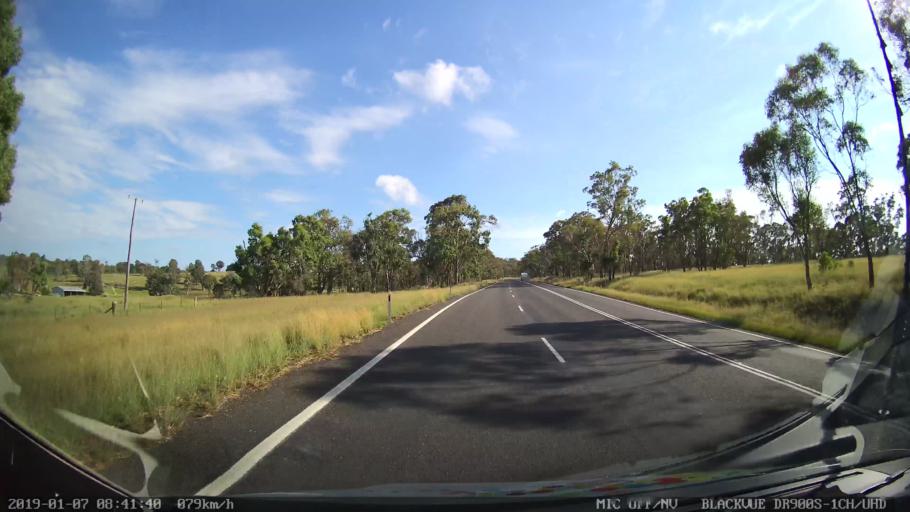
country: AU
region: New South Wales
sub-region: Tamworth Municipality
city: Kootingal
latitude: -30.8647
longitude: 151.2041
